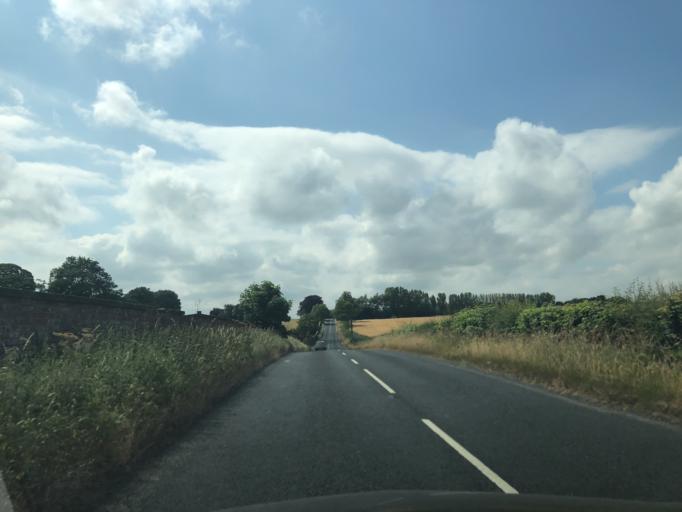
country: GB
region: England
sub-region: North Yorkshire
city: Stokesley
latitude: 54.4577
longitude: -1.2597
